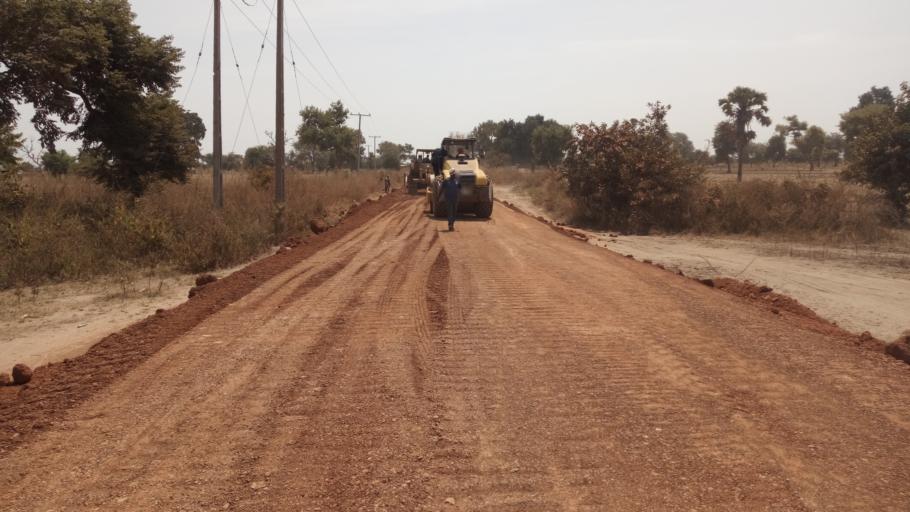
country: NG
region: Adamawa
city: Yola
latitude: 9.2270
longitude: 12.8787
